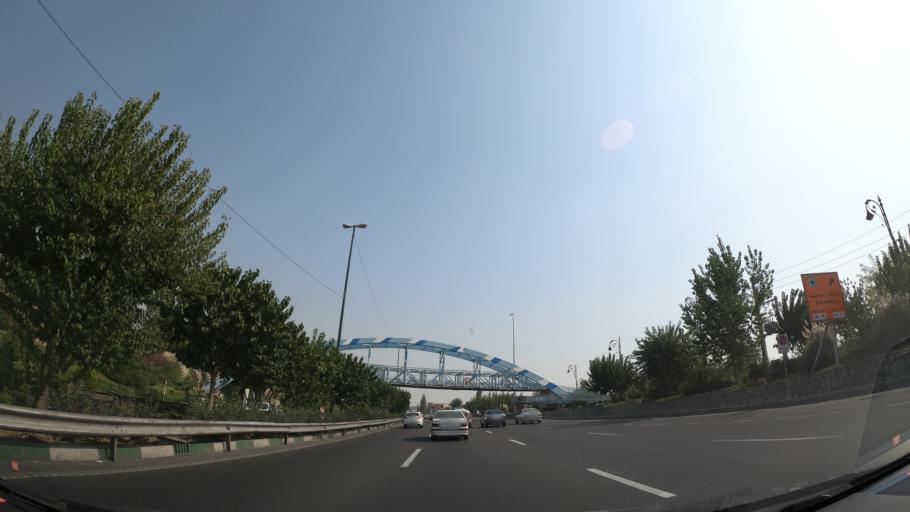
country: IR
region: Tehran
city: Tehran
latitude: 35.7543
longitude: 51.2723
